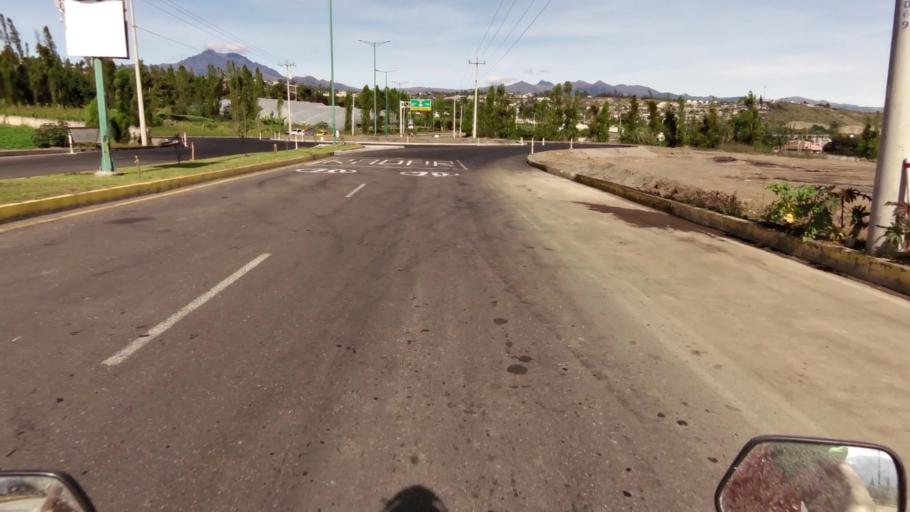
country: EC
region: Imbabura
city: Ibarra
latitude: 0.3329
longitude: -78.1553
